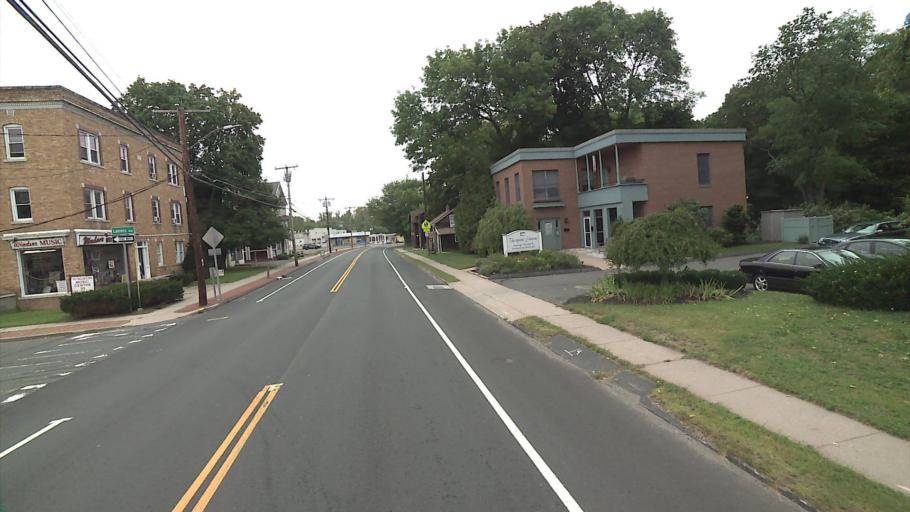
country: US
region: Connecticut
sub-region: Hartford County
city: Windsor
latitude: 41.8548
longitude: -72.6478
